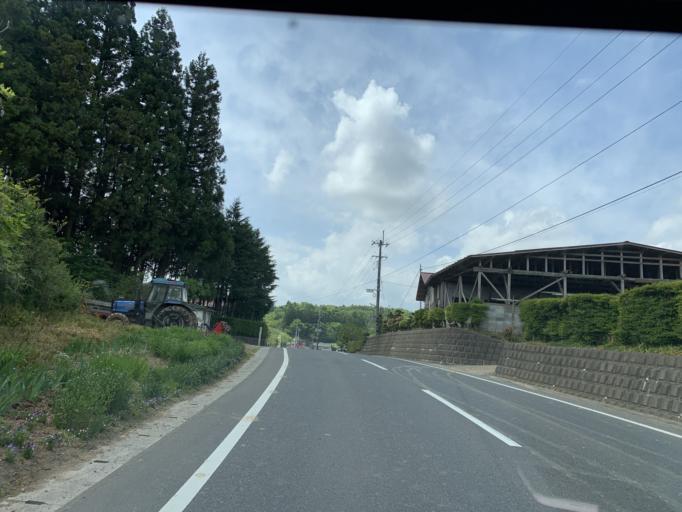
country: JP
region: Iwate
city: Ichinoseki
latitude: 38.7900
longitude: 141.0021
